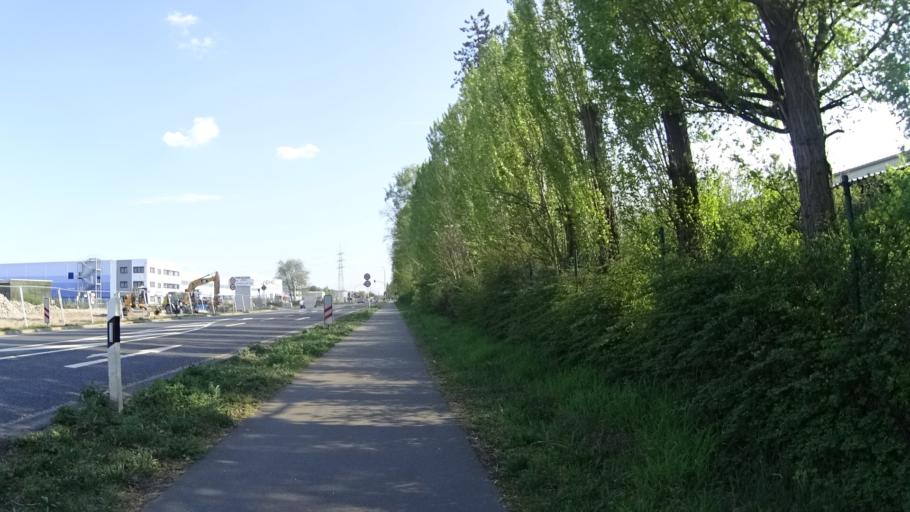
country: DE
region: North Rhine-Westphalia
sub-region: Regierungsbezirk Dusseldorf
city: Dormagen
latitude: 51.1329
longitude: 6.8034
